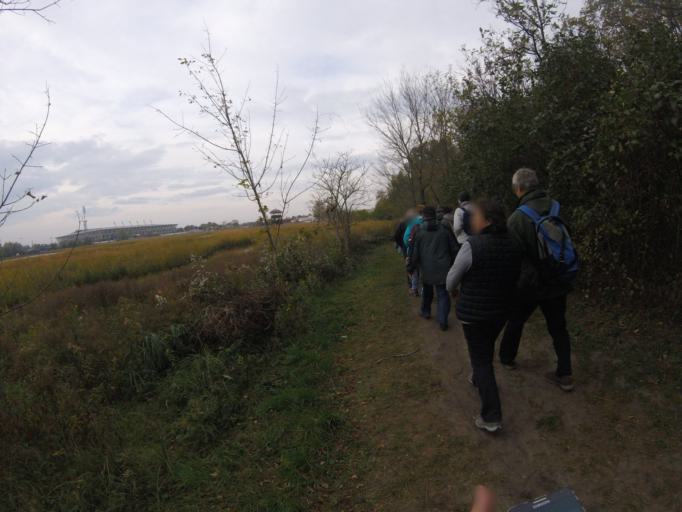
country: HU
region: Fejer
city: Szekesfehervar
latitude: 47.1693
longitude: 18.4193
